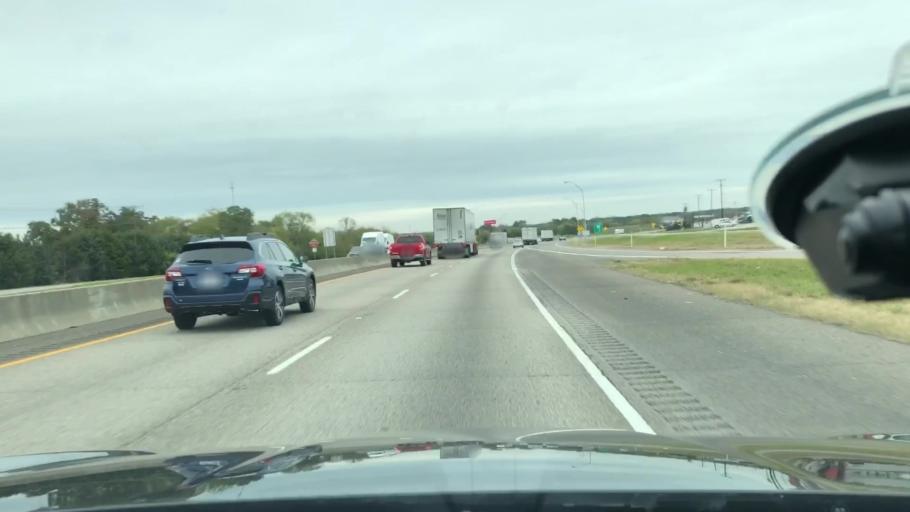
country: US
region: Texas
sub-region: Hopkins County
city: Sulphur Springs
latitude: 33.1381
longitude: -95.5716
